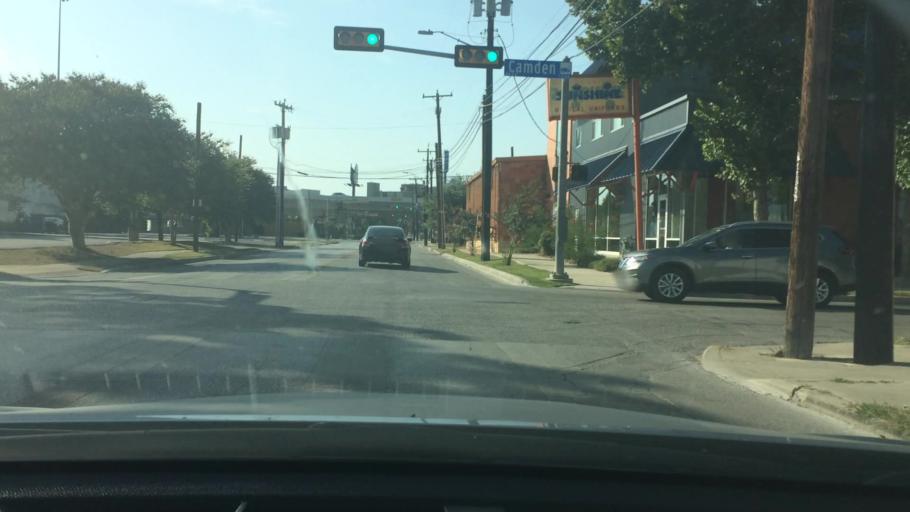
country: US
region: Texas
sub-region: Bexar County
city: San Antonio
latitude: 29.4367
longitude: -98.4882
